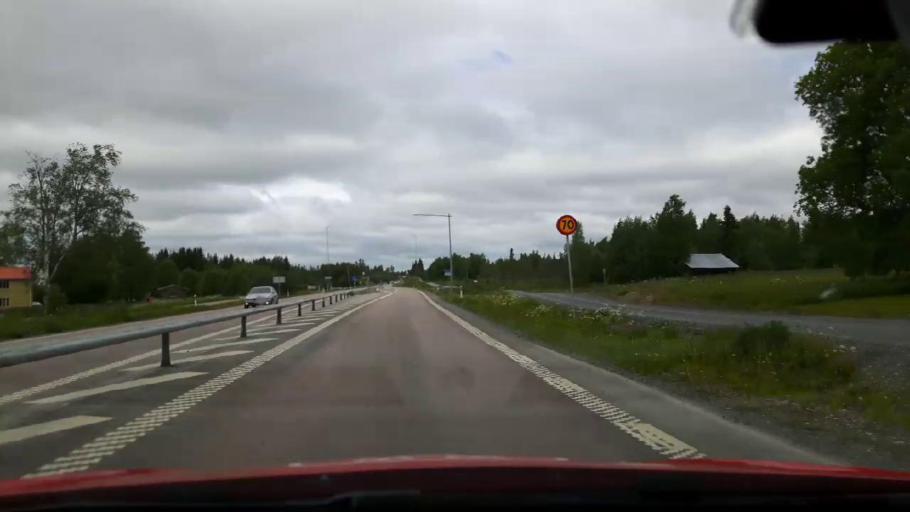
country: SE
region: Jaemtland
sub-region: Krokoms Kommun
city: Krokom
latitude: 63.2851
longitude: 14.5157
